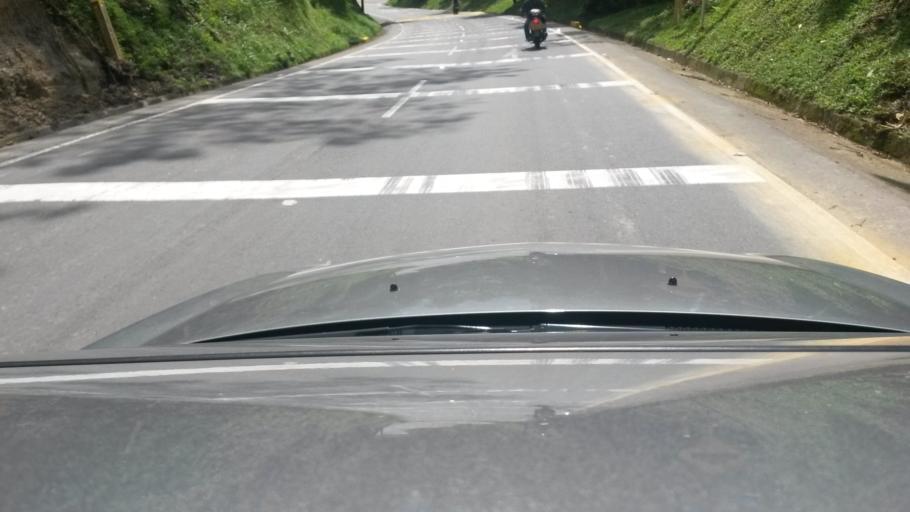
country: CO
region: Caldas
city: Chinchina
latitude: 5.0006
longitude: -75.5957
